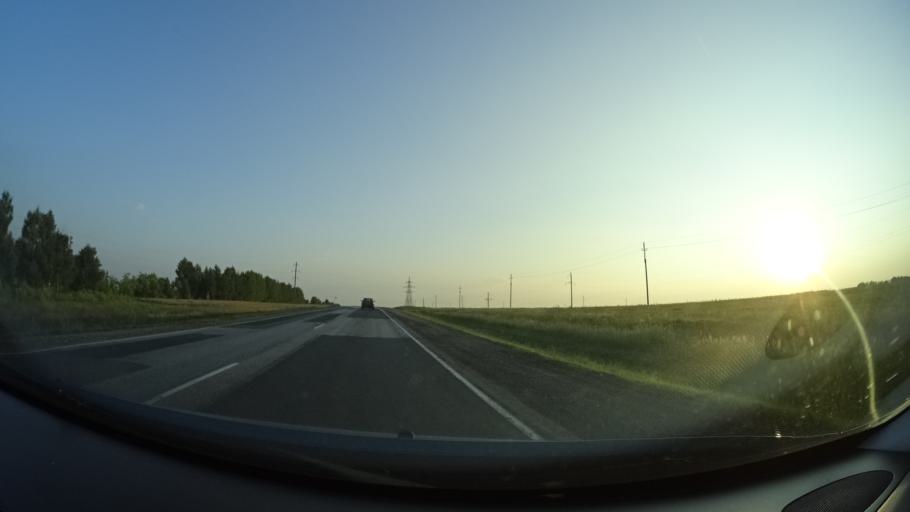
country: RU
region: Samara
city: Sernovodsk
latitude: 53.9387
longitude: 51.3484
